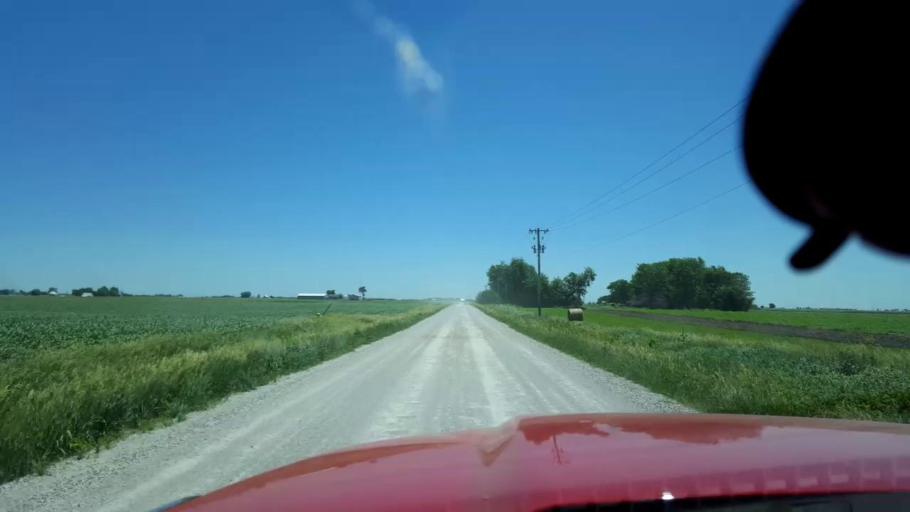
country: US
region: Iowa
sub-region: Washington County
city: Washington
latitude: 41.2799
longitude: -91.6568
